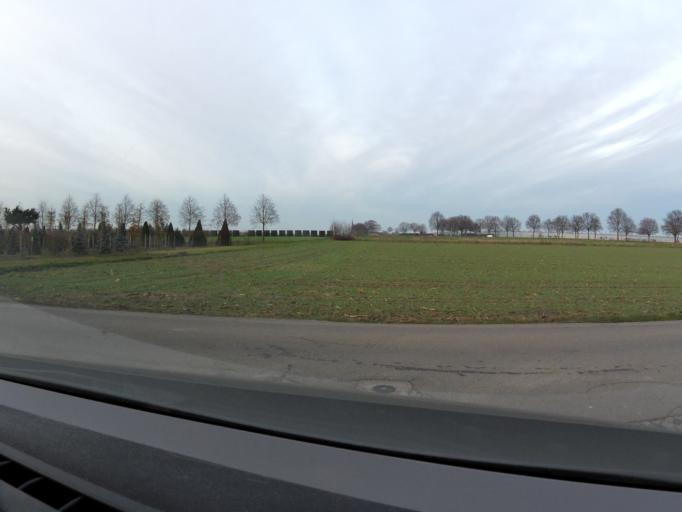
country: DE
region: North Rhine-Westphalia
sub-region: Regierungsbezirk Dusseldorf
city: Nettetal
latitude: 51.3261
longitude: 6.2265
